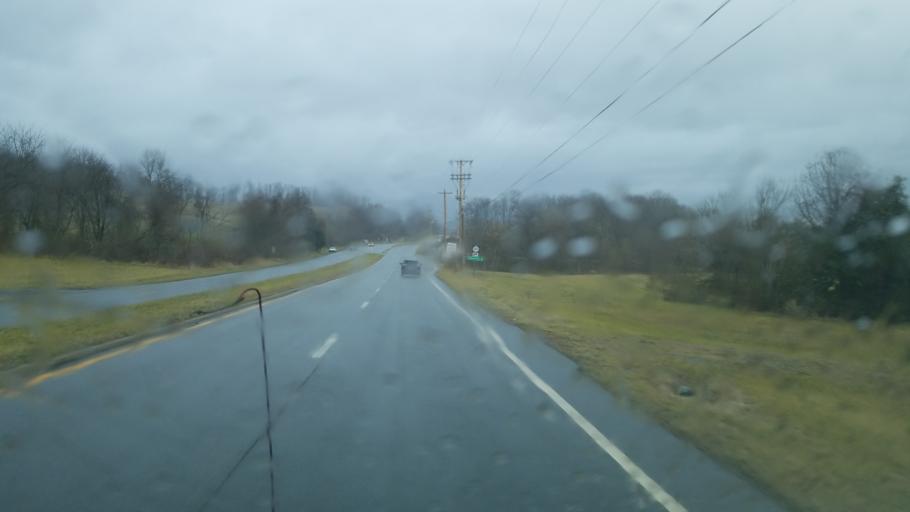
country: US
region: Virginia
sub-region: Giles County
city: Pearisburg
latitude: 37.3149
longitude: -80.7325
